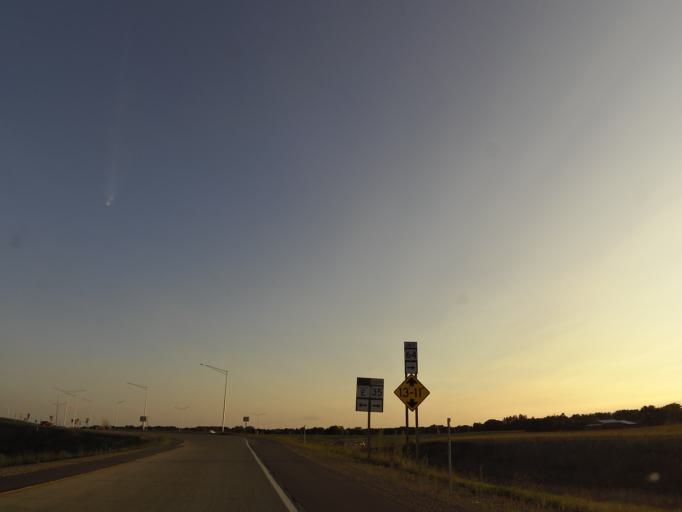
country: US
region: Minnesota
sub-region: Washington County
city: Stillwater
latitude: 45.0615
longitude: -92.7821
